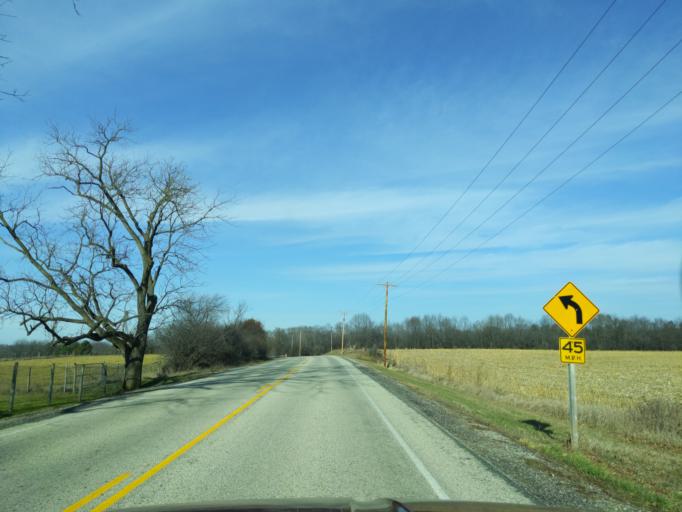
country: US
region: Wisconsin
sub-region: Walworth County
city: Elkhorn
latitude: 42.7470
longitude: -88.5925
